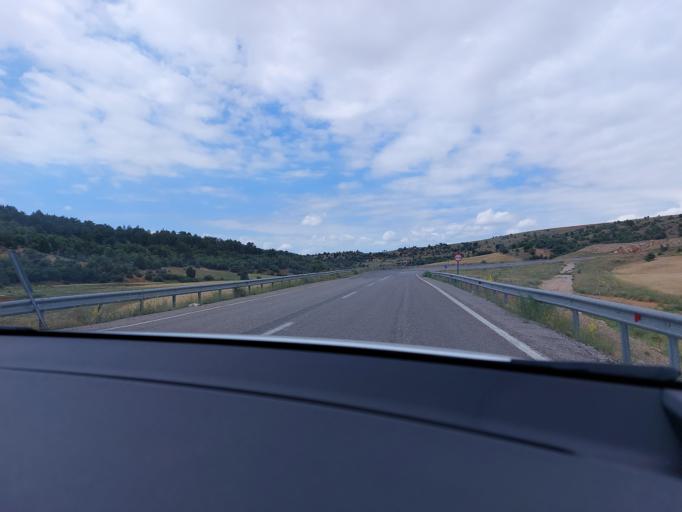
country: TR
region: Konya
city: Doganbey
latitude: 37.8950
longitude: 31.8025
